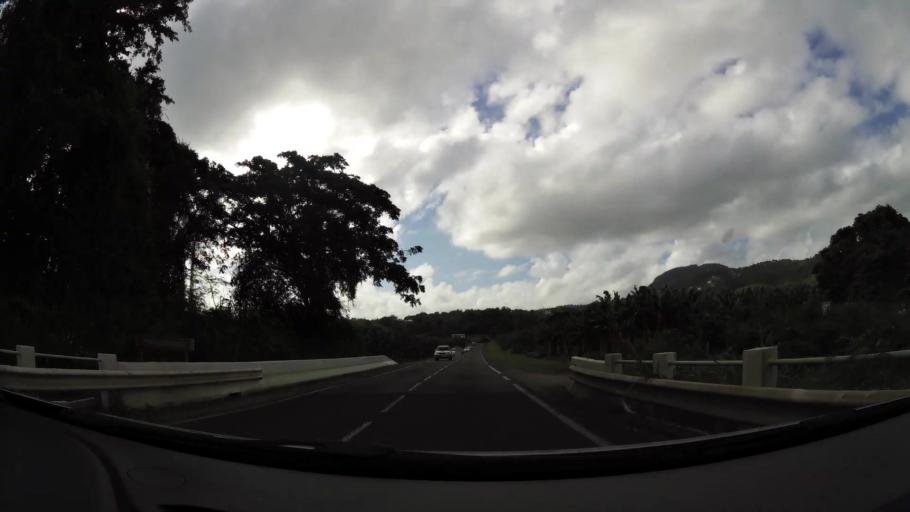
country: MQ
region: Martinique
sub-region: Martinique
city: Le Francois
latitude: 14.5852
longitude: -60.8701
